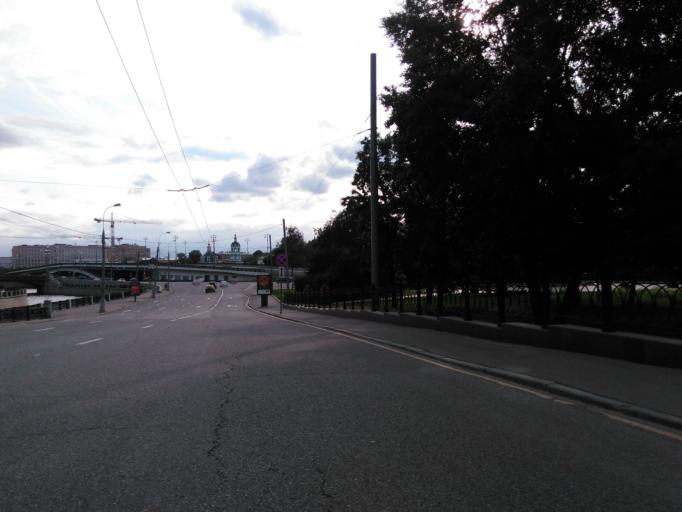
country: RU
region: Moscow
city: Zamoskvorech'ye
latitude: 55.7489
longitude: 37.6438
